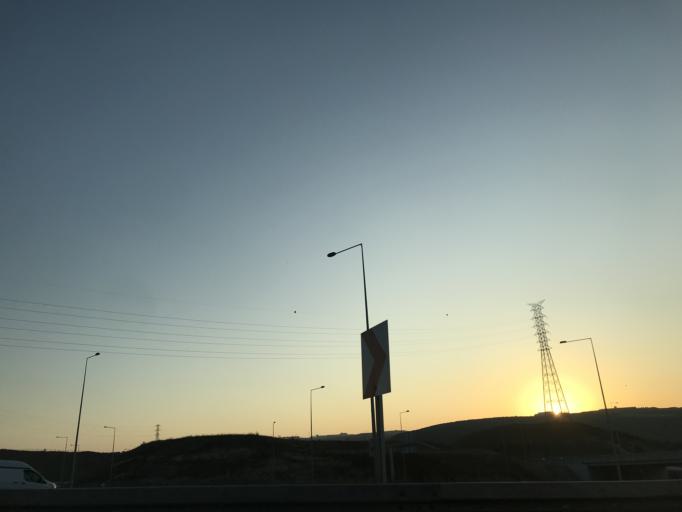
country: TR
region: Kocaeli
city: Tavsanli
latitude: 40.8104
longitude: 29.5183
